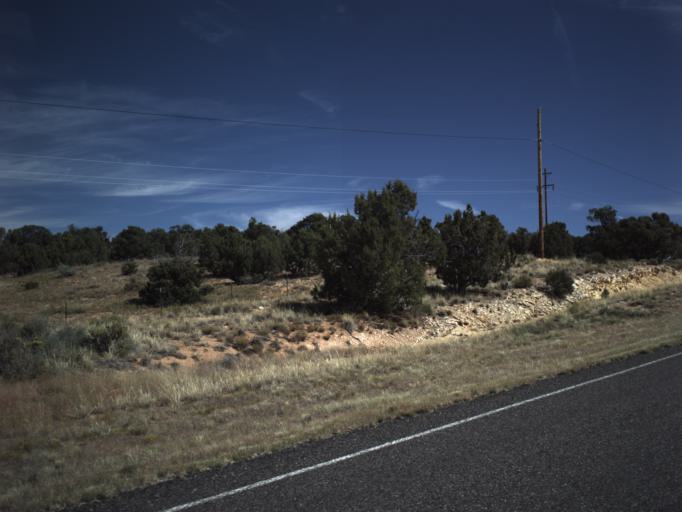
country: US
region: Utah
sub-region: Wayne County
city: Loa
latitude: 37.7497
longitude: -111.4794
